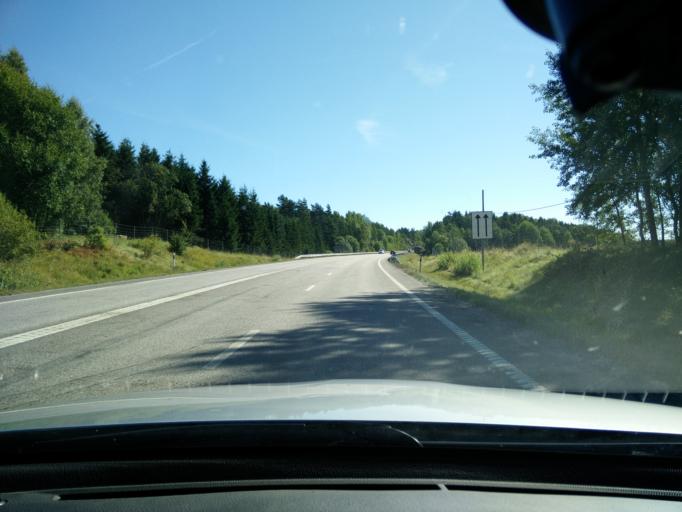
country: SE
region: Stockholm
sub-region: Lidingo
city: Brevik
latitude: 59.4535
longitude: 18.1963
